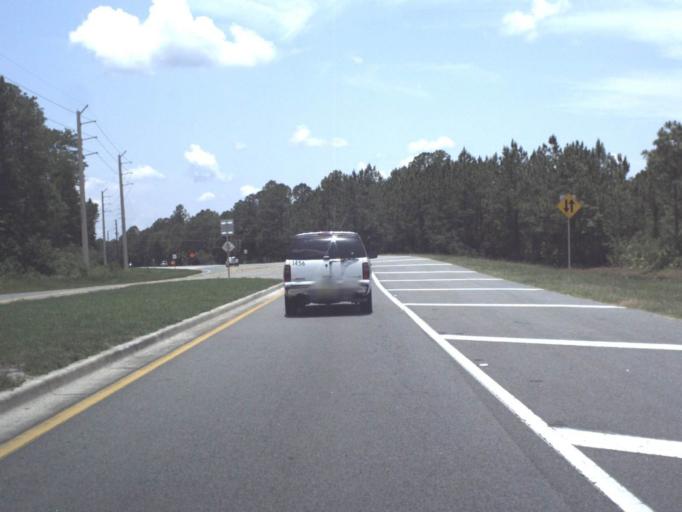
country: US
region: Florida
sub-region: Saint Johns County
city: Saint Augustine
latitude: 29.9268
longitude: -81.4215
